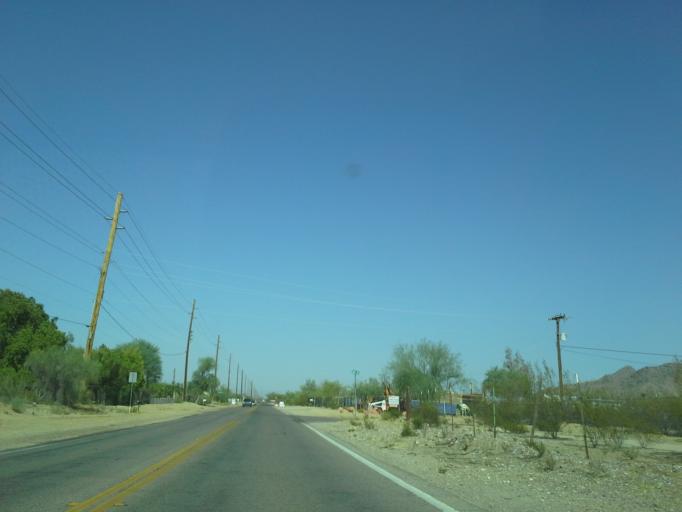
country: US
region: Arizona
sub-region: Maricopa County
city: Queen Creek
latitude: 33.2047
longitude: -111.6714
